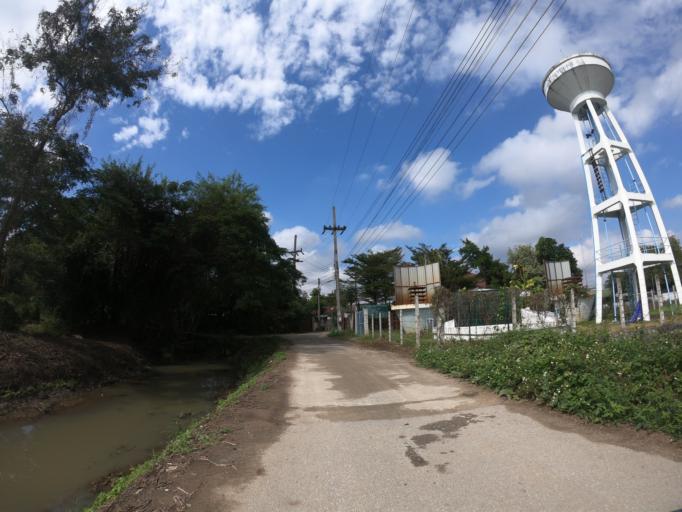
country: TH
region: Chiang Mai
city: Saraphi
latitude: 18.6985
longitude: 98.9779
